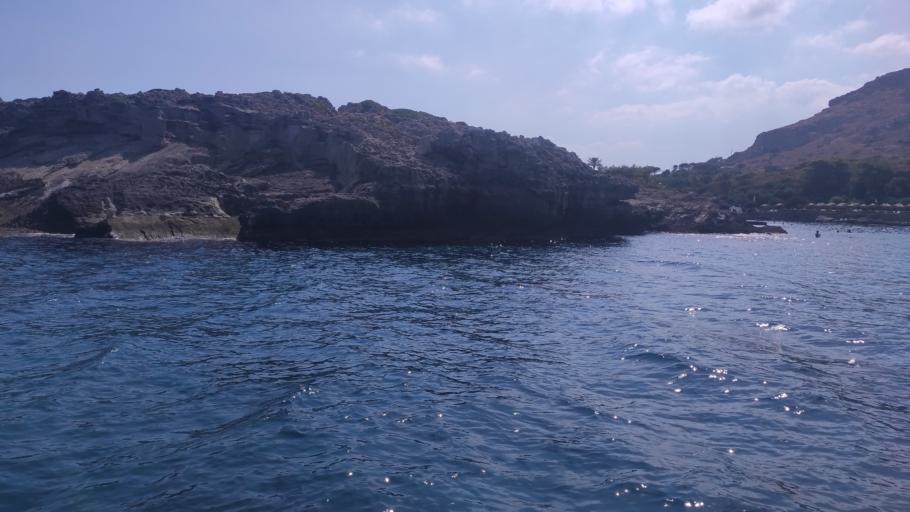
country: GR
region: South Aegean
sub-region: Nomos Dodekanisou
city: Faliraki
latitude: 36.3791
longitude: 28.2404
